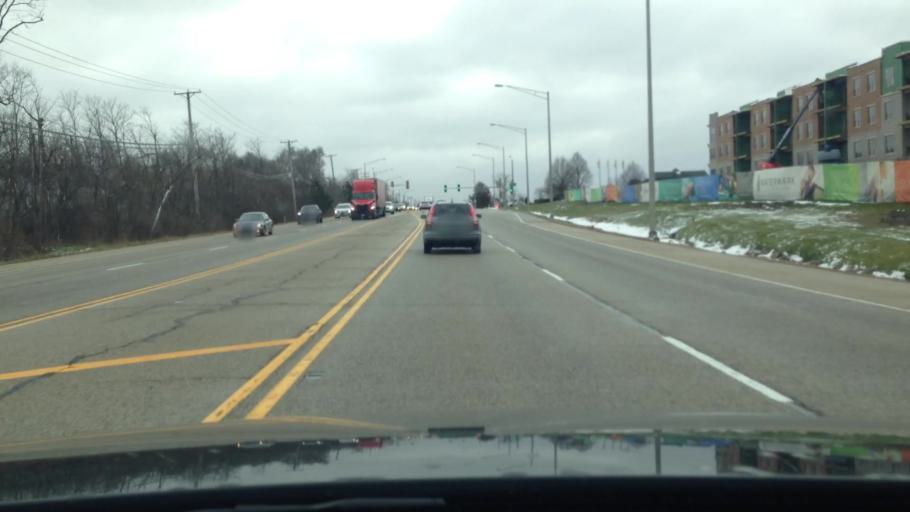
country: US
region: Illinois
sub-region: Kane County
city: Sleepy Hollow
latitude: 42.0967
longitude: -88.3352
